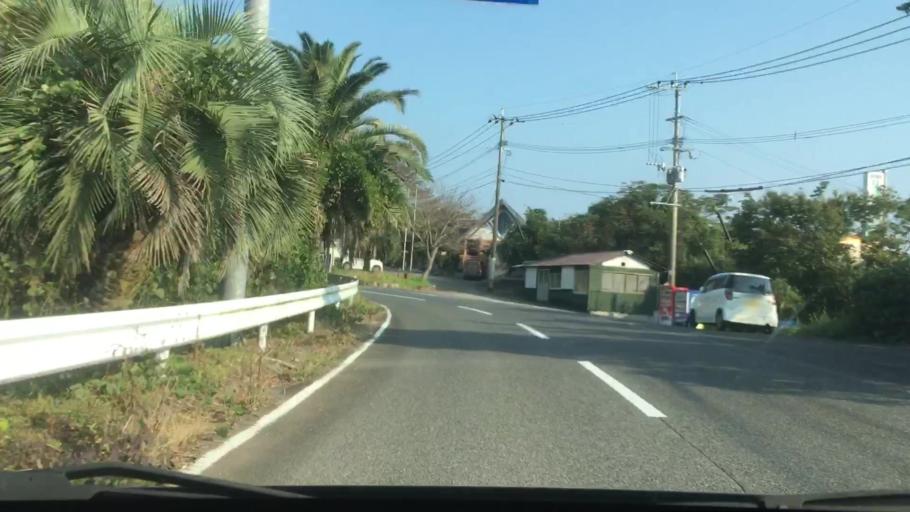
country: JP
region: Nagasaki
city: Sasebo
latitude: 33.0416
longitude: 129.6959
